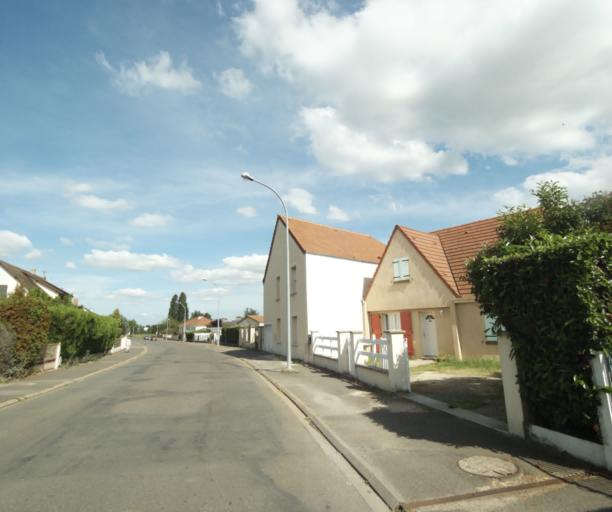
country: FR
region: Centre
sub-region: Departement d'Eure-et-Loir
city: Luce
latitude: 48.4319
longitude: 1.4527
